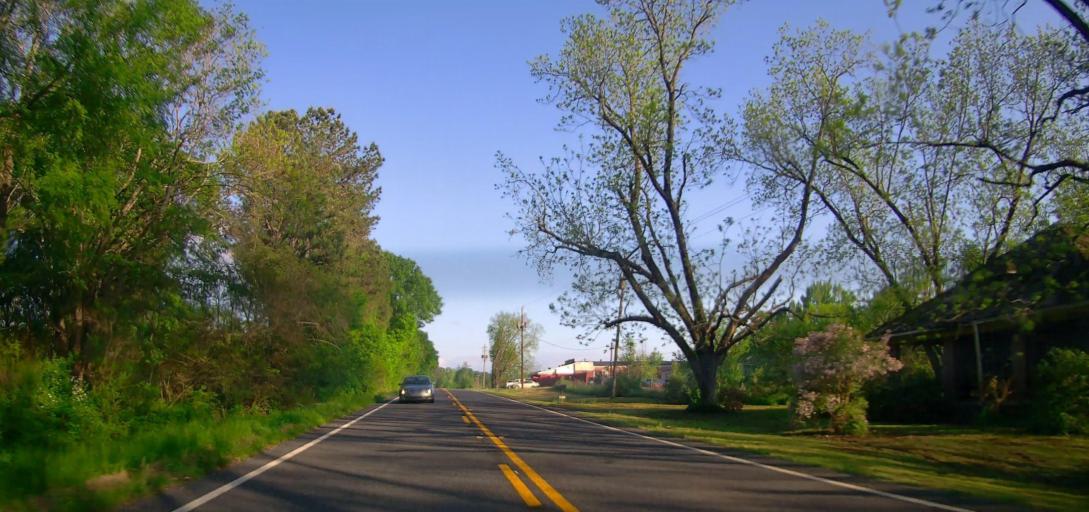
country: US
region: Georgia
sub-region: Jasper County
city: Monticello
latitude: 33.4440
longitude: -83.6236
